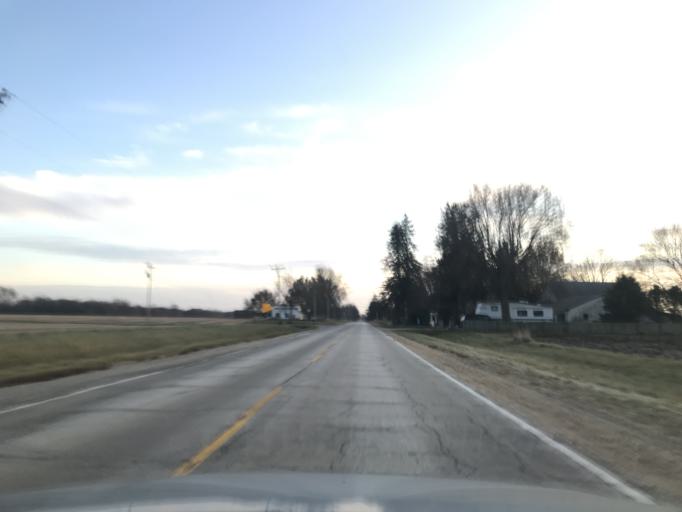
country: US
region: Illinois
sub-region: Henderson County
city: Oquawka
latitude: 40.9430
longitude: -90.8641
